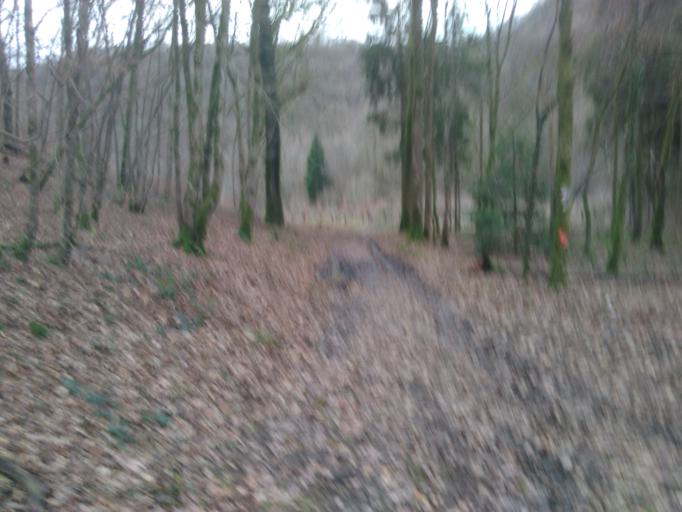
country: BE
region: Wallonia
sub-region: Province de Namur
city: Houyet
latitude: 50.1963
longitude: 4.9561
